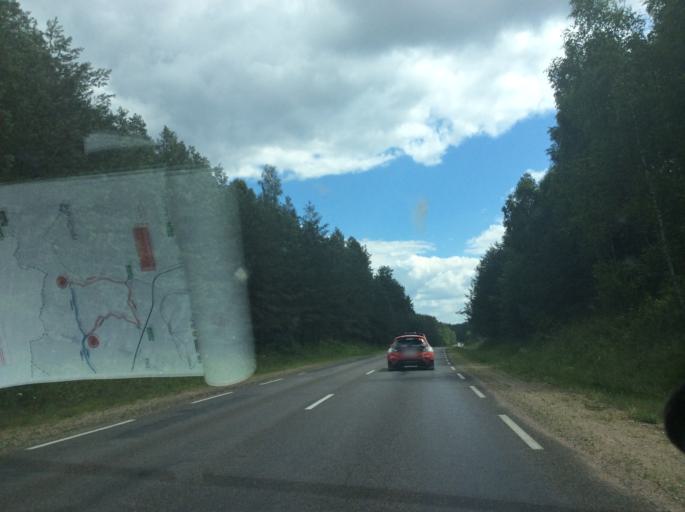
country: LT
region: Alytaus apskritis
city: Druskininkai
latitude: 54.0453
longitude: 23.9423
